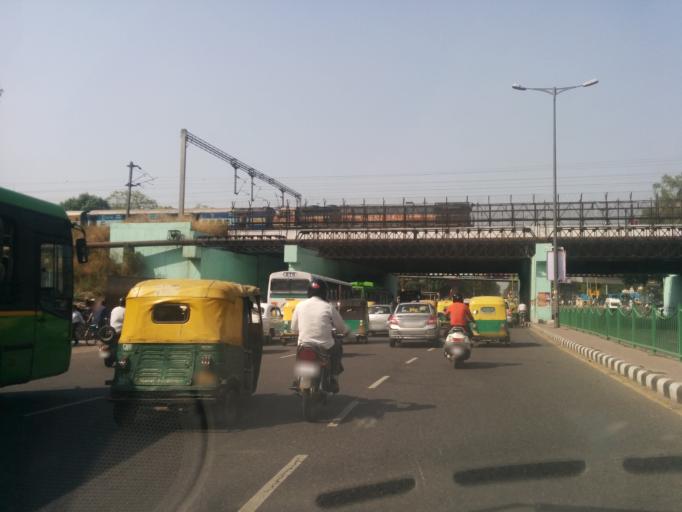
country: IN
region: NCT
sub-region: New Delhi
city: New Delhi
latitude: 28.6265
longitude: 77.2413
